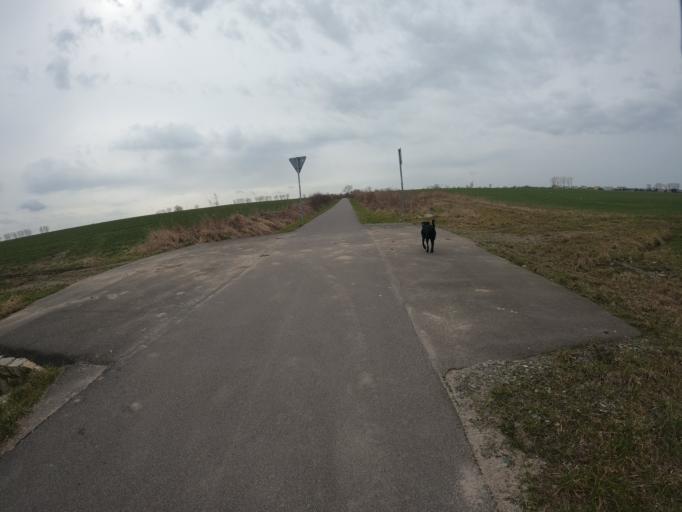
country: PL
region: West Pomeranian Voivodeship
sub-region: Powiat gryficki
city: Trzebiatow
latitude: 54.0993
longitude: 15.2821
